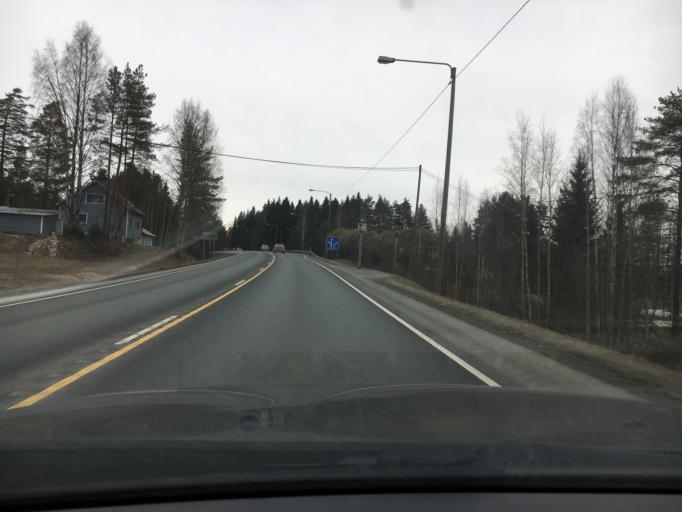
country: FI
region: Northern Savo
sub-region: Kuopio
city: Siilinjaervi
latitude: 63.1129
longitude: 27.6439
